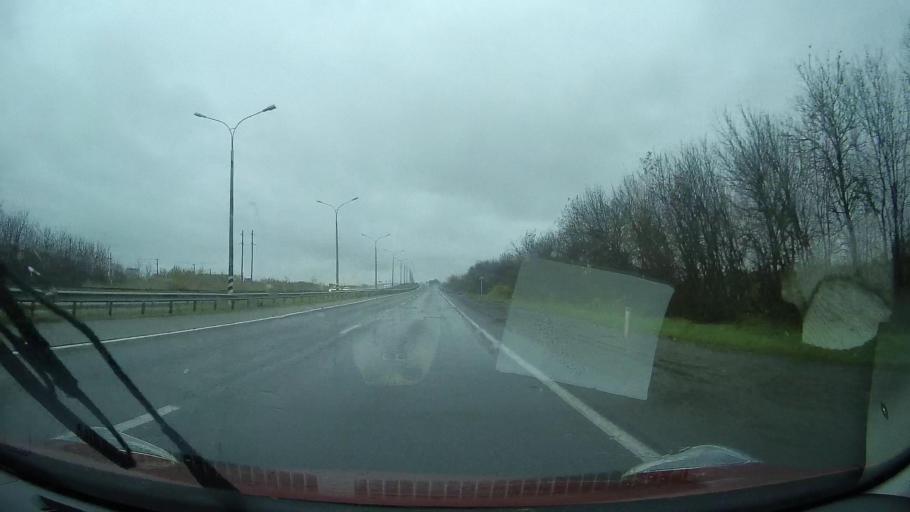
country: RU
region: Stavropol'skiy
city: Nevinnomyssk
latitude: 44.6354
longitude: 42.0003
